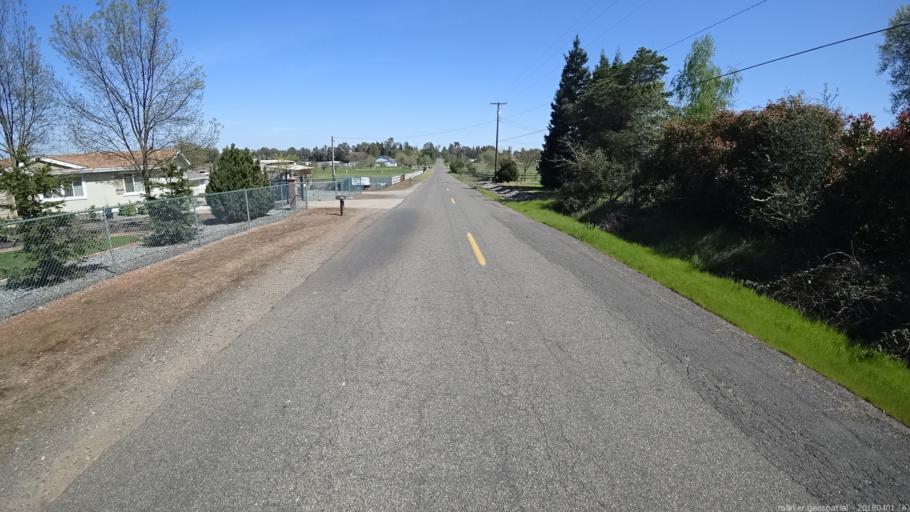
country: US
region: California
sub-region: Sacramento County
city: Wilton
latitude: 38.3941
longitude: -121.2234
